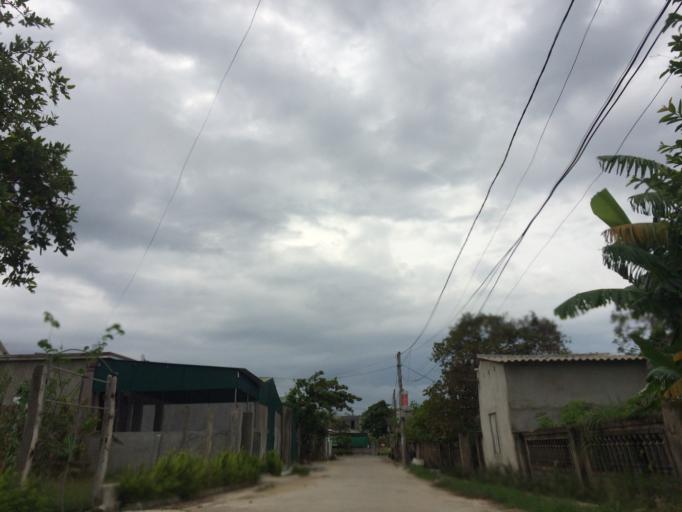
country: VN
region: Ha Tinh
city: Thach Ha
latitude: 18.3665
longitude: 105.8880
